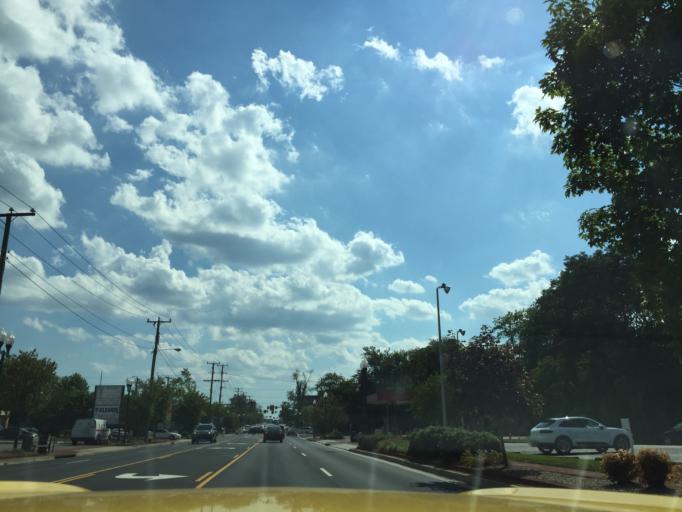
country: US
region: Virginia
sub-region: Fairfax County
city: Vienna
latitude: 38.9083
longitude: -77.2569
